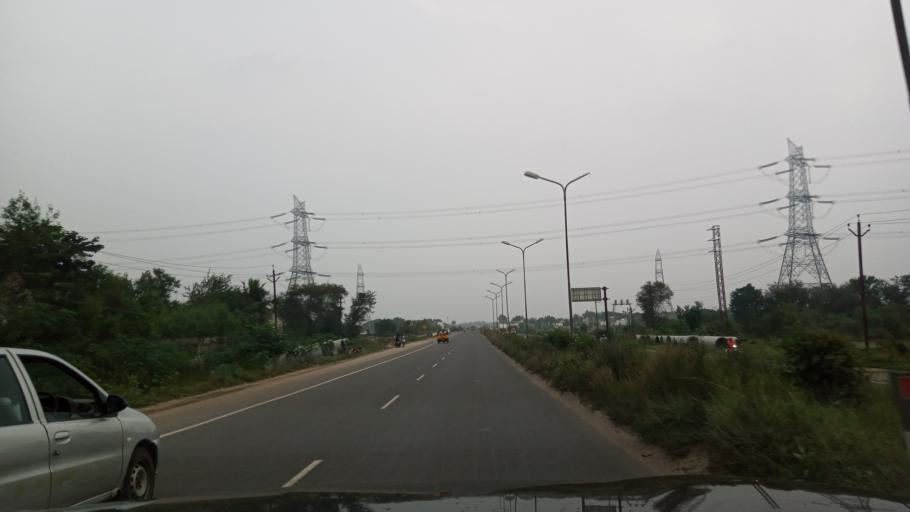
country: IN
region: Tamil Nadu
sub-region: Vellore
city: Walajapet
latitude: 12.9078
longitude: 79.4113
